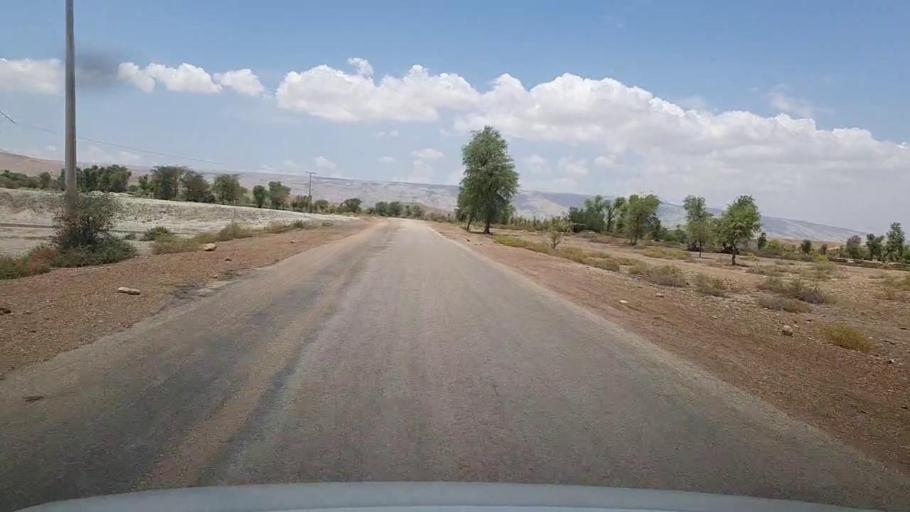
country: PK
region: Sindh
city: Bhan
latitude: 26.3163
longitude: 67.5819
